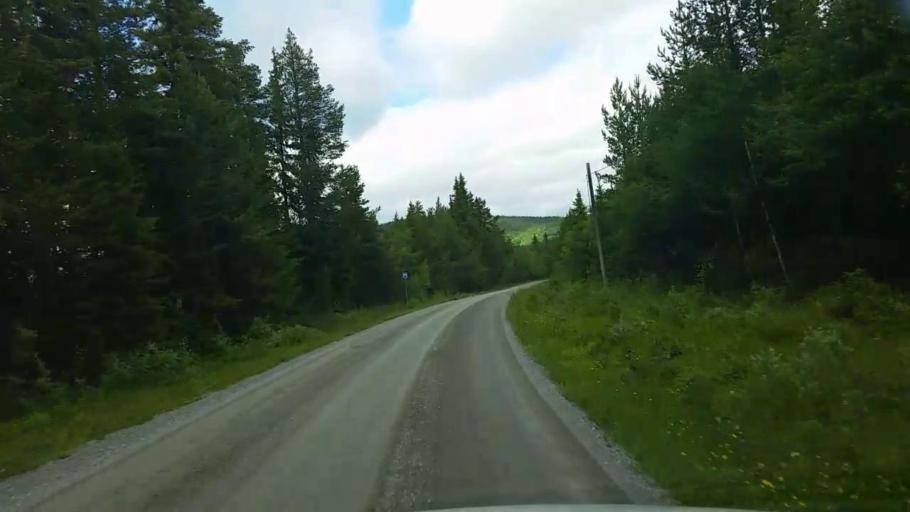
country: NO
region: Hedmark
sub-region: Engerdal
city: Engerdal
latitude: 62.4214
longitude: 12.6748
